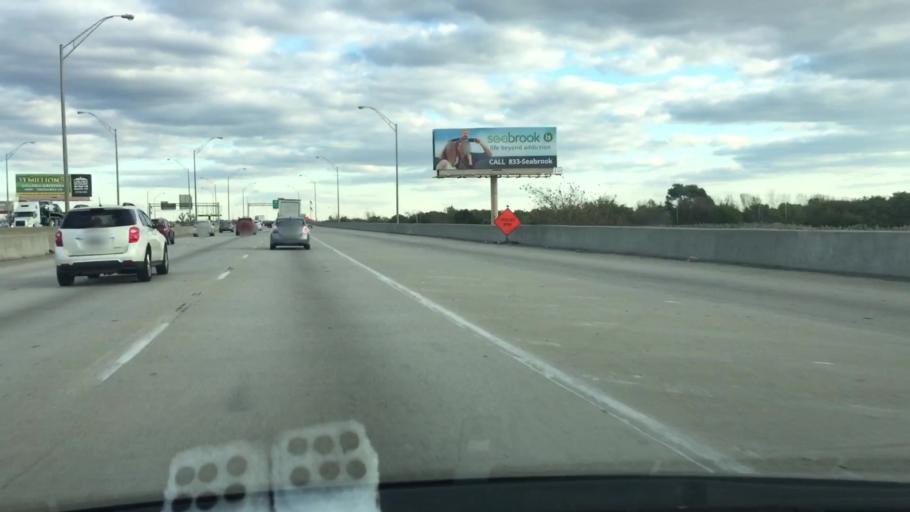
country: US
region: Pennsylvania
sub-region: Delaware County
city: Colwyn
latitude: 39.8889
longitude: -75.2185
